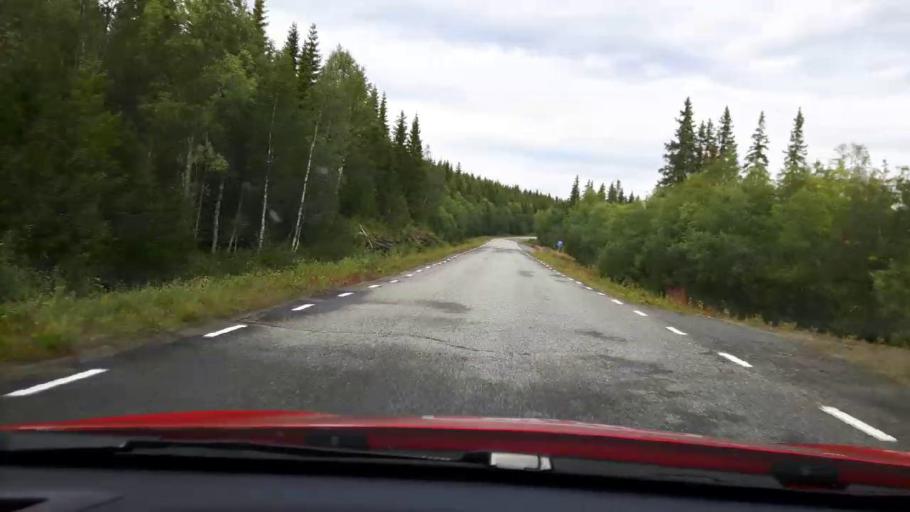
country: SE
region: Jaemtland
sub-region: Are Kommun
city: Are
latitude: 63.7197
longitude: 12.9681
